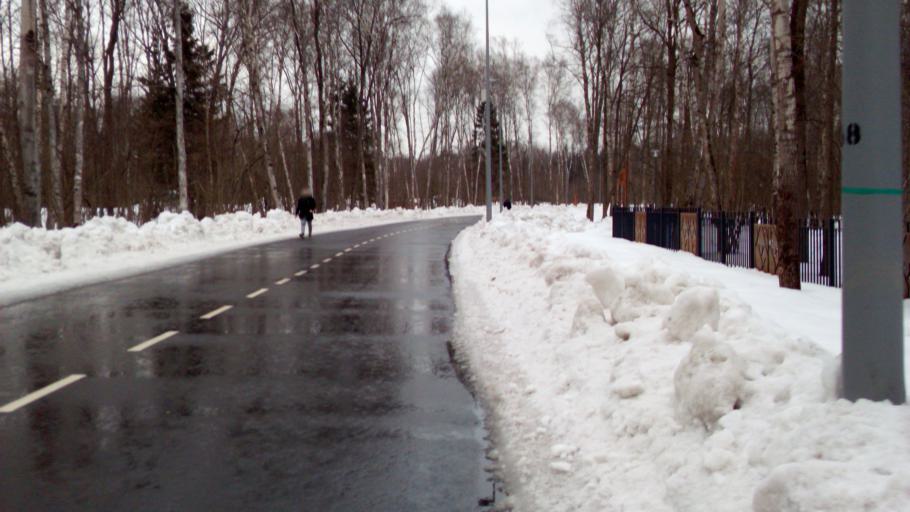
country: RU
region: Moskovskaya
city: Moskovskiy
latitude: 55.6017
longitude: 37.3858
